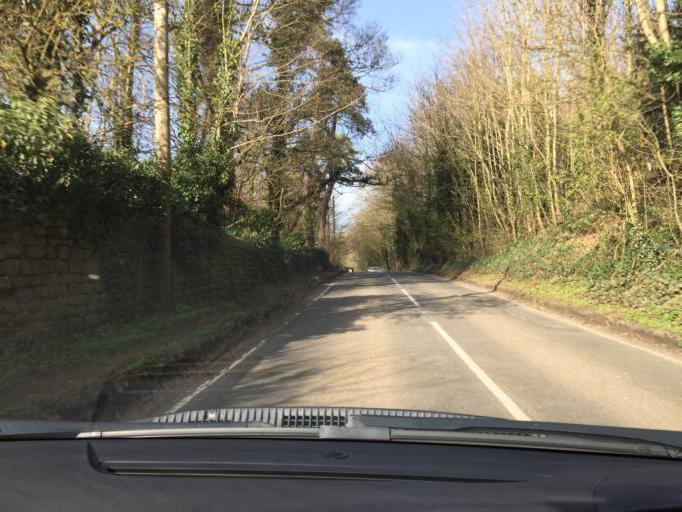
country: GB
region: England
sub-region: Oxfordshire
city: Bloxham
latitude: 52.0399
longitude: -1.3905
